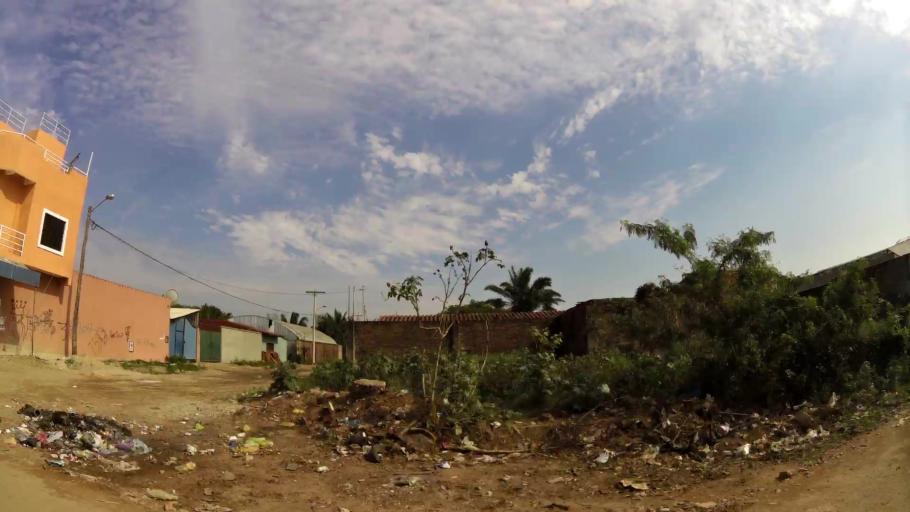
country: BO
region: Santa Cruz
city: Santa Cruz de la Sierra
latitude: -17.7237
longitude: -63.1365
